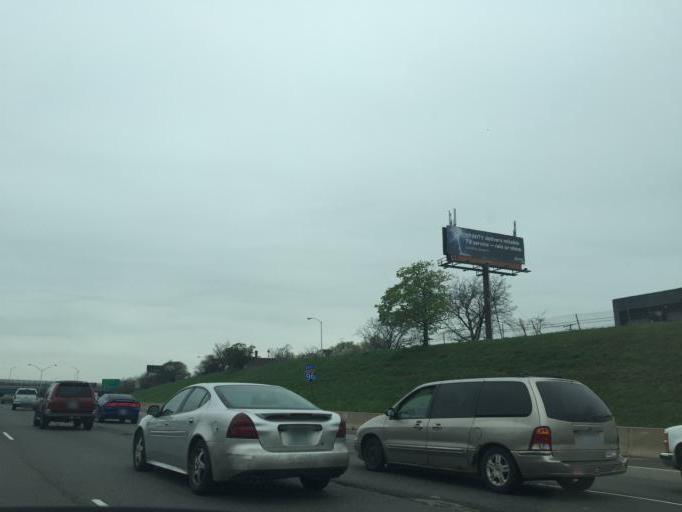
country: US
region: Michigan
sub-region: Wayne County
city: Highland Park
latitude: 42.3800
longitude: -83.1464
